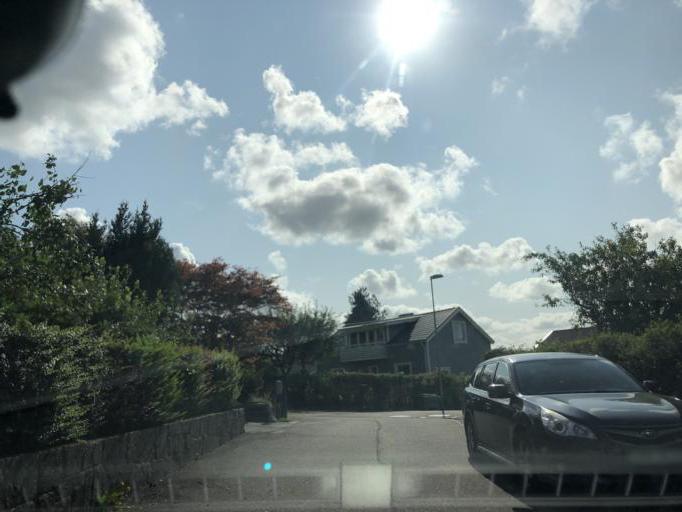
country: SE
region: Vaestra Goetaland
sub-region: Goteborg
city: Goeteborg
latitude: 57.7359
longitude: 11.9615
